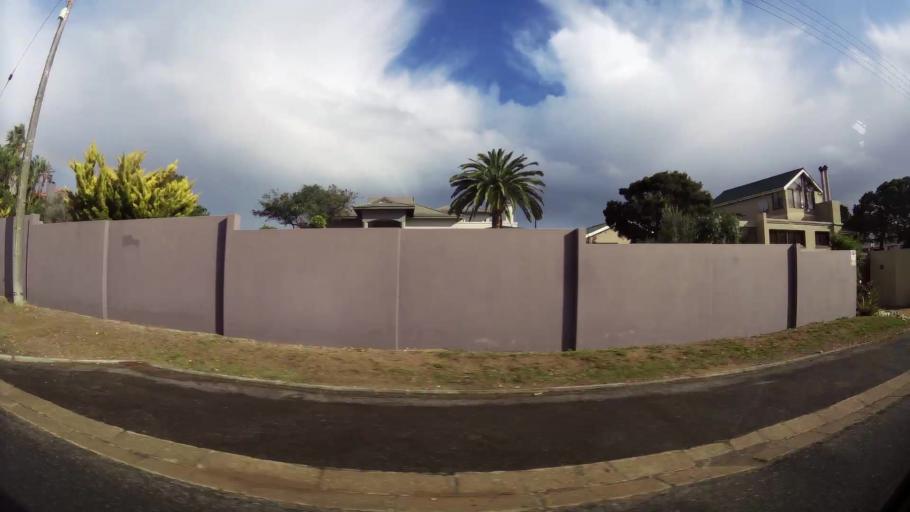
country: ZA
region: Western Cape
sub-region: Eden District Municipality
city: Mossel Bay
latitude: -34.1901
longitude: 22.1381
